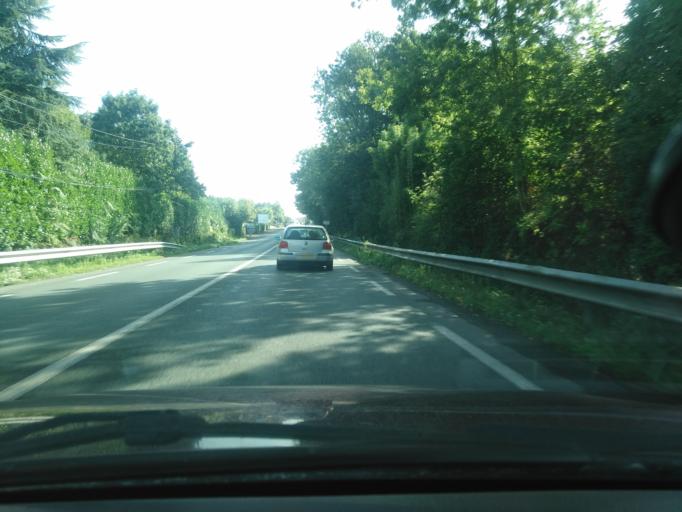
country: FR
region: Pays de la Loire
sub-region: Departement de la Vendee
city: La Ferriere
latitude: 46.7089
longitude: -1.3225
